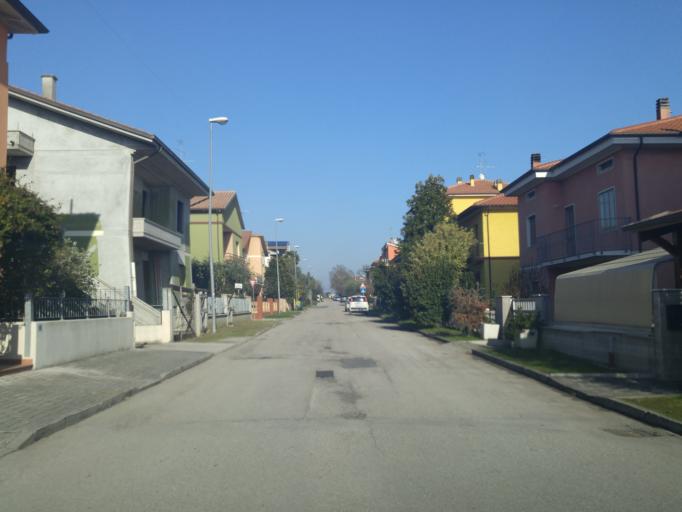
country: IT
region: The Marches
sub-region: Provincia di Pesaro e Urbino
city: Calcinelli
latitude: 43.7612
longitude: 12.9256
